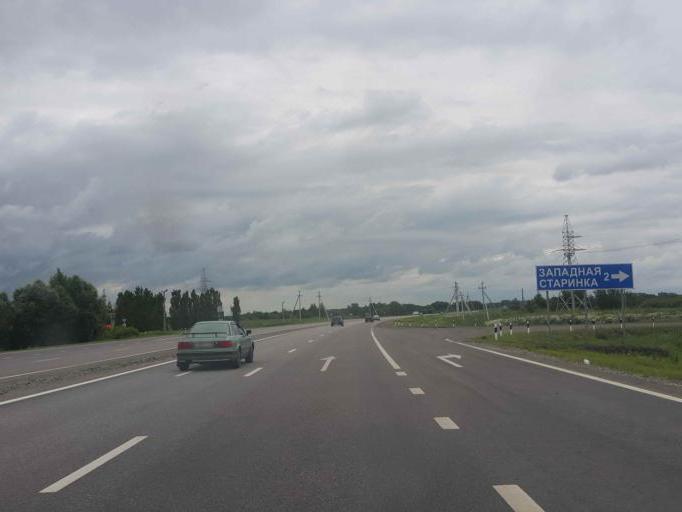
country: RU
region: Tambov
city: Zavoronezhskoye
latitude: 52.8755
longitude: 40.7518
